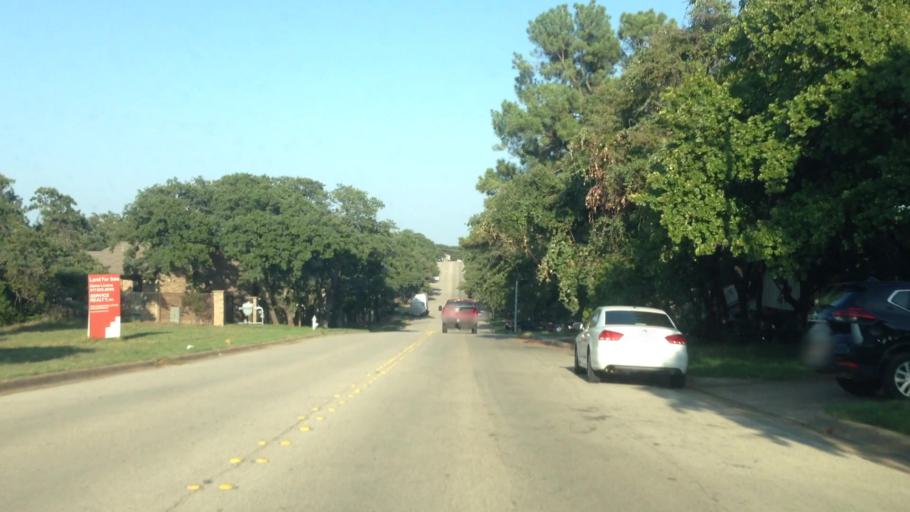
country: US
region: Texas
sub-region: Tarrant County
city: Pantego
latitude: 32.7546
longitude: -97.1968
